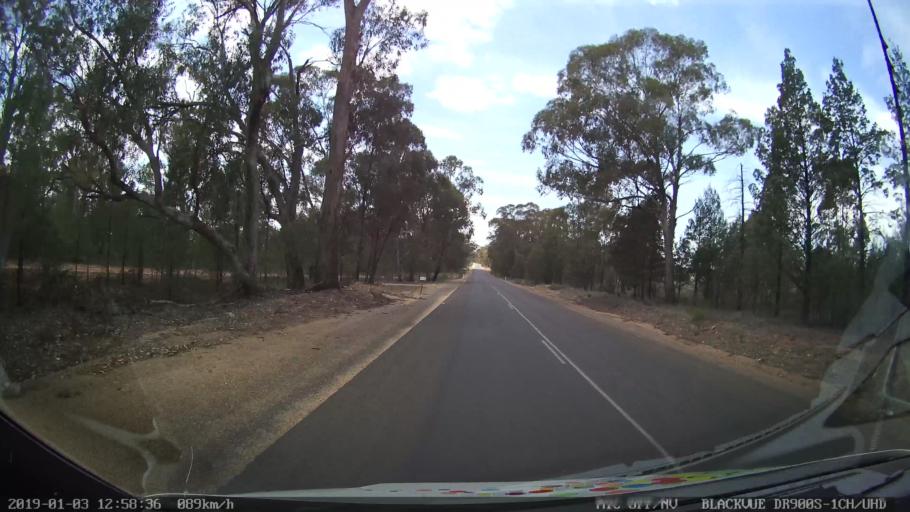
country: AU
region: New South Wales
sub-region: Cabonne
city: Canowindra
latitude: -33.6409
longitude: 148.3774
